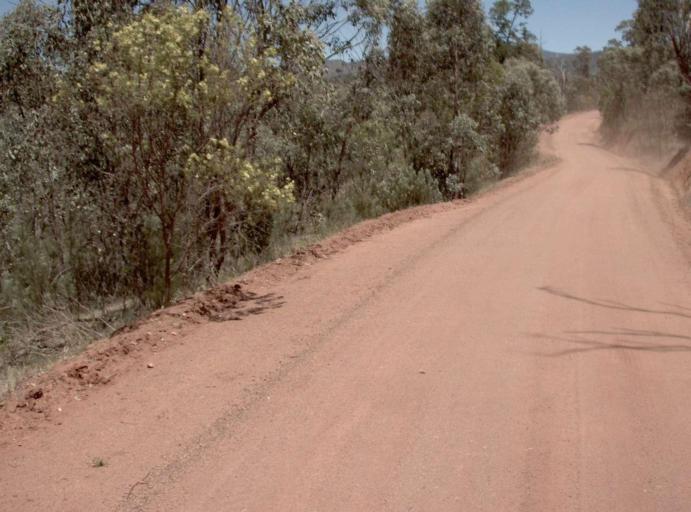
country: AU
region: New South Wales
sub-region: Snowy River
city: Jindabyne
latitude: -36.9185
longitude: 148.4192
